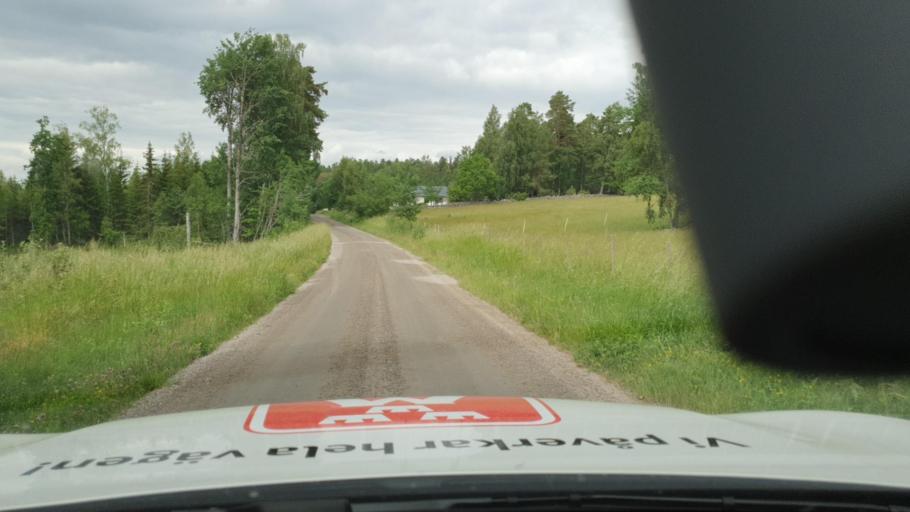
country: SE
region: Vaestra Goetaland
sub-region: Tidaholms Kommun
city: Olofstorp
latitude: 58.1837
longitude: 14.0491
